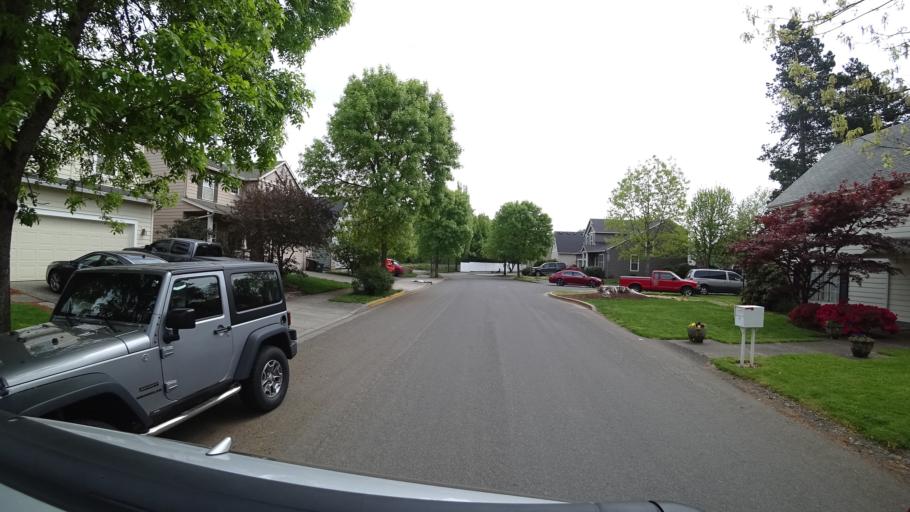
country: US
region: Oregon
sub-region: Washington County
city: Hillsboro
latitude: 45.5364
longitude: -122.9955
